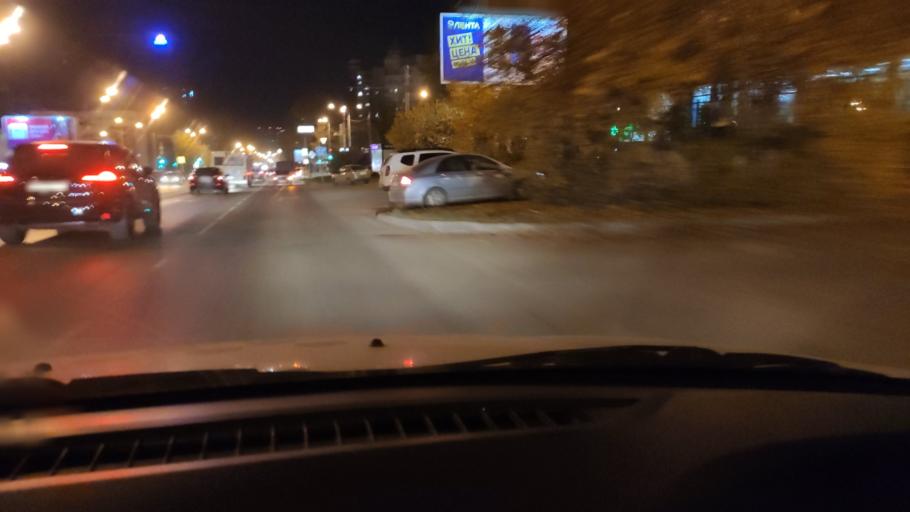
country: RU
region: Perm
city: Perm
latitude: 57.9849
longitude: 56.2171
